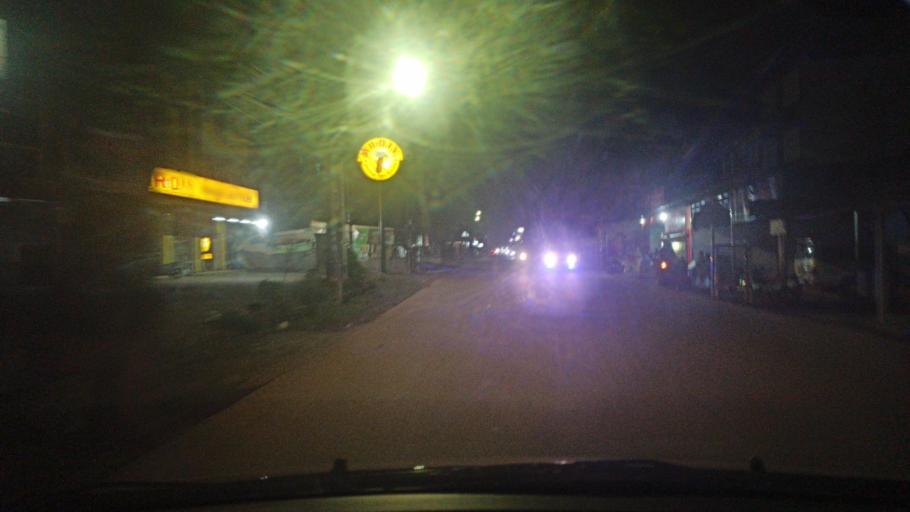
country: ID
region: South Sumatra
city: Palembang
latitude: -2.9406
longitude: 104.7833
